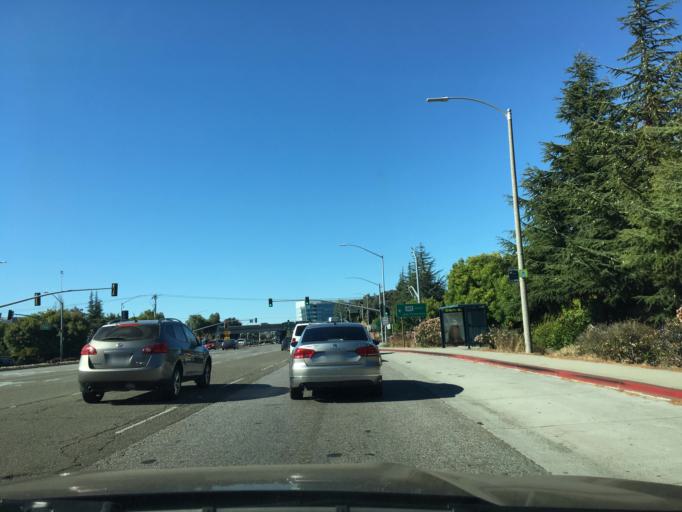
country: US
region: California
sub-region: Santa Clara County
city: Sunnyvale
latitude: 37.4012
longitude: -122.0270
